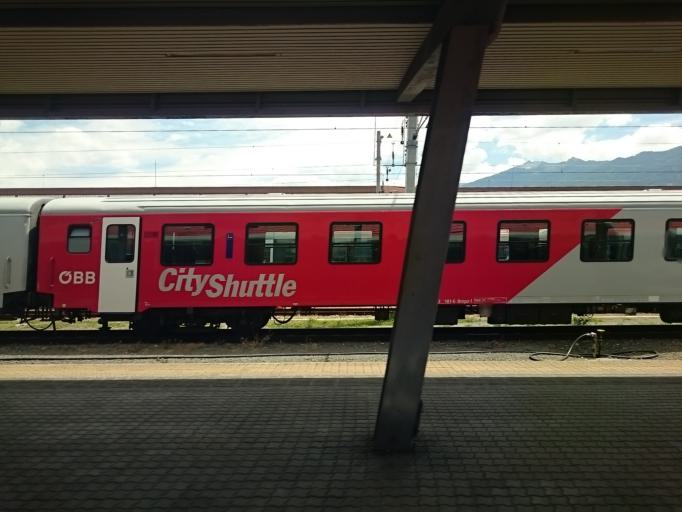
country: AT
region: Tyrol
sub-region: Innsbruck Stadt
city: Innsbruck
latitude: 47.2617
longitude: 11.4007
